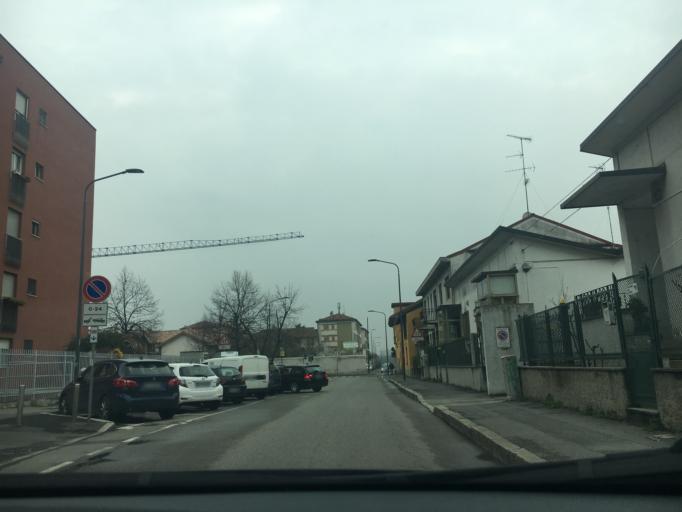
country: IT
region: Lombardy
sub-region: Citta metropolitana di Milano
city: Pero
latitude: 45.4924
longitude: 9.1010
